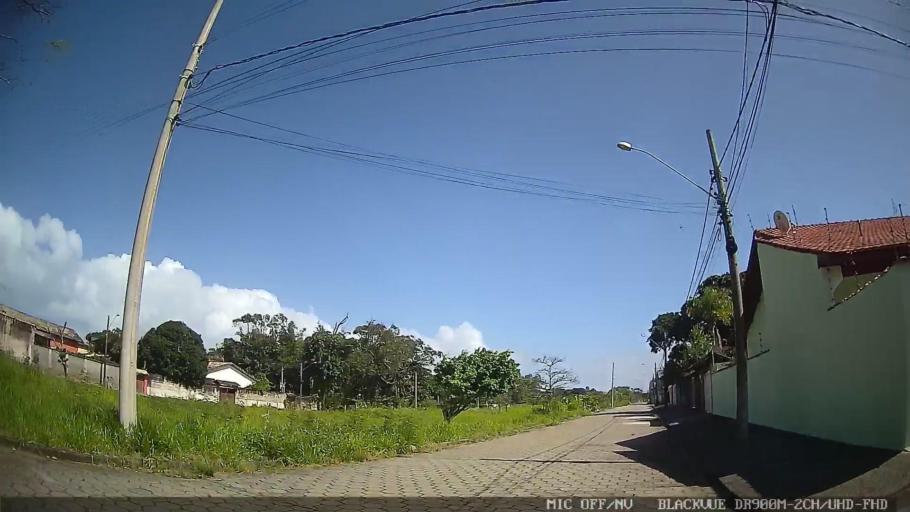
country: BR
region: Sao Paulo
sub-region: Itanhaem
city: Itanhaem
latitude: -24.1653
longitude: -46.7566
